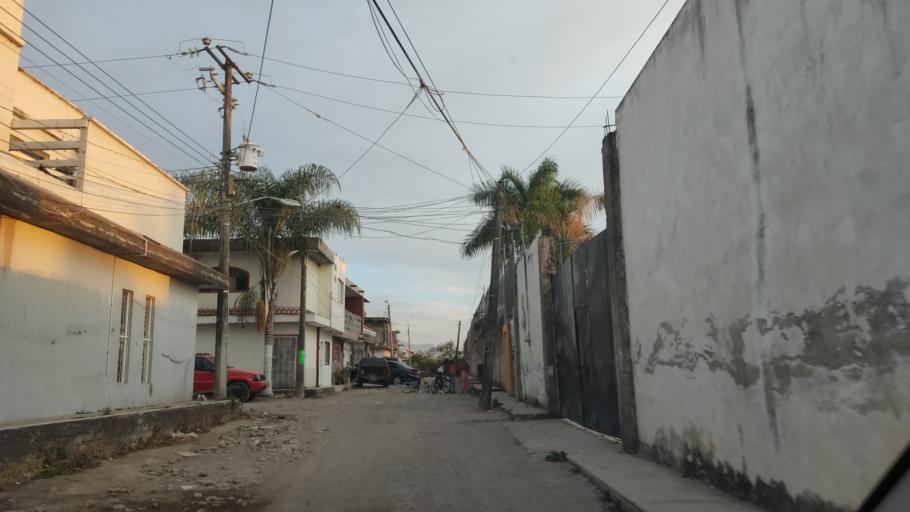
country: MX
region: Nayarit
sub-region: Tepic
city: La Corregidora
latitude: 21.4476
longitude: -104.8154
